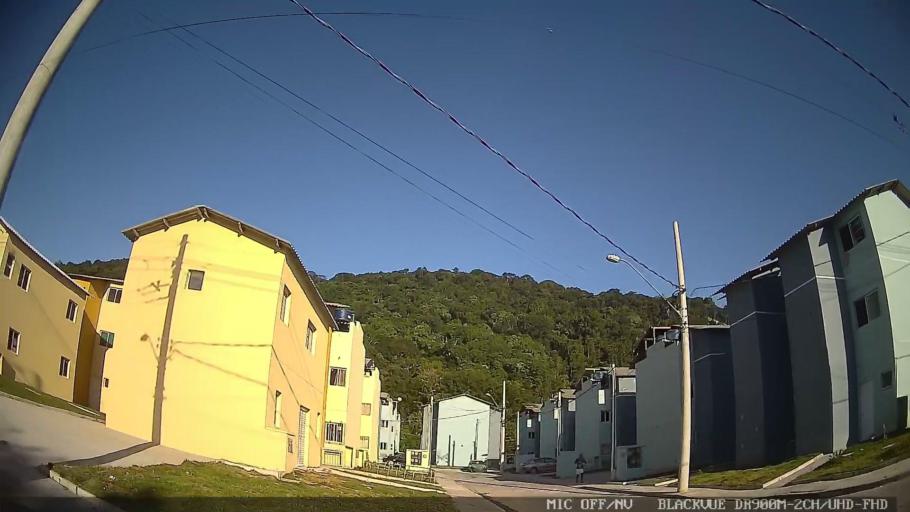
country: BR
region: Sao Paulo
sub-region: Guaruja
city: Guaruja
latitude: -23.9674
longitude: -46.2432
